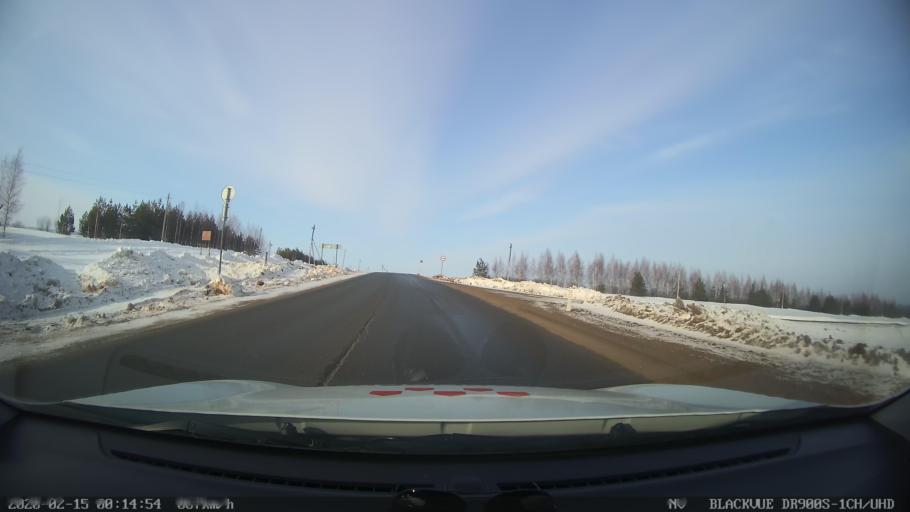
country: RU
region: Tatarstan
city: Stolbishchi
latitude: 55.4912
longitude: 49.0047
